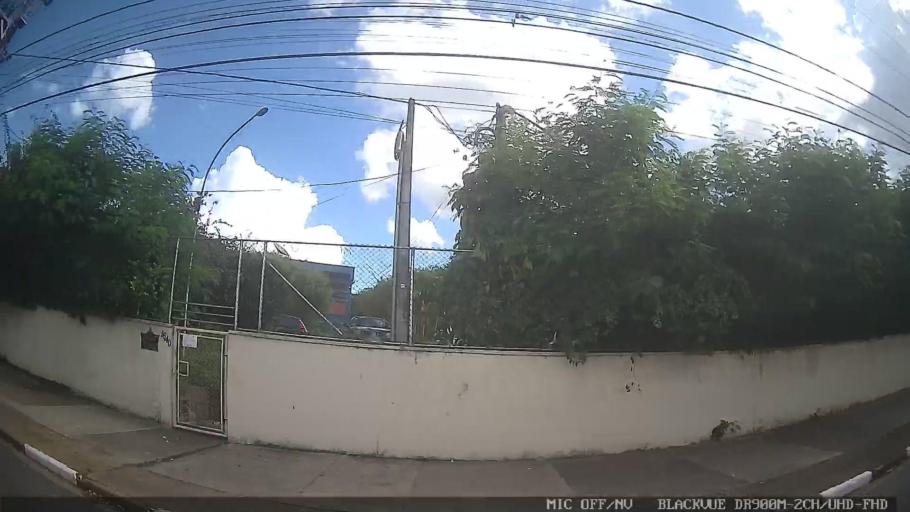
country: BR
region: Sao Paulo
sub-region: Atibaia
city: Atibaia
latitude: -23.1123
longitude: -46.5446
